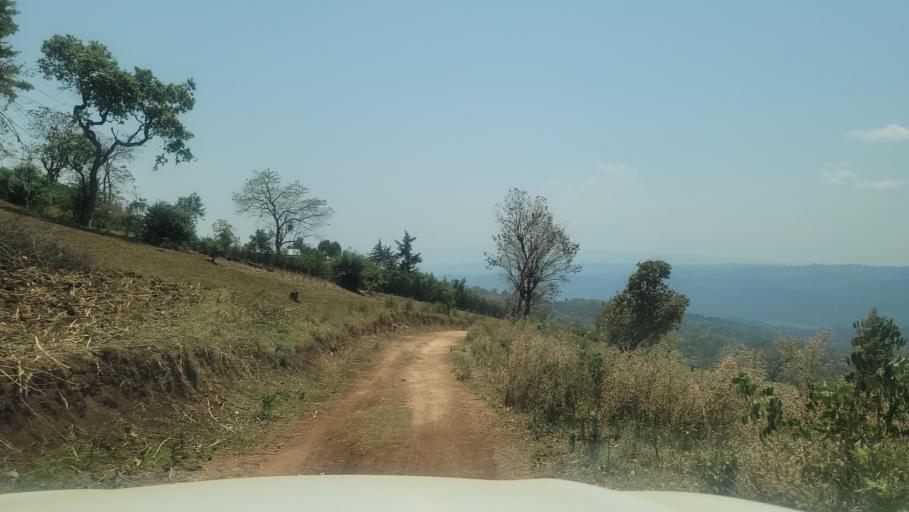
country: ET
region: Southern Nations, Nationalities, and People's Region
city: Bonga
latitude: 7.5301
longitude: 36.1905
